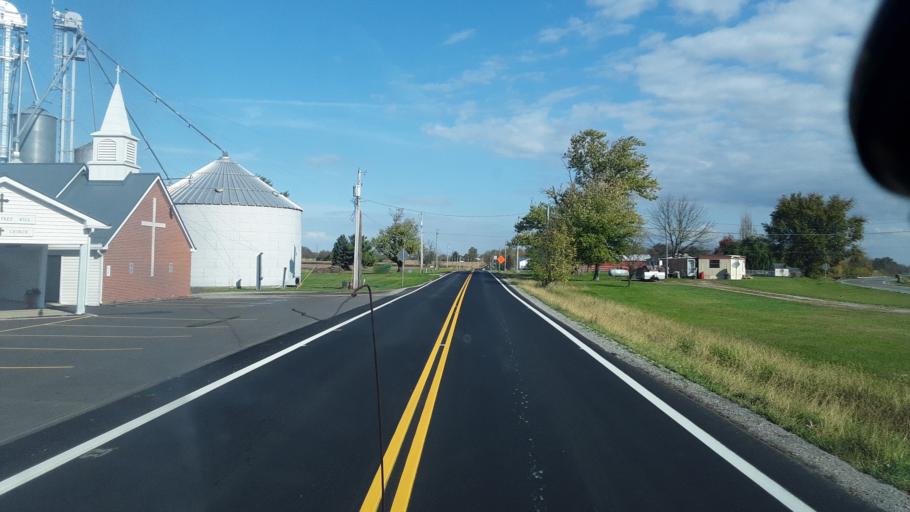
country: US
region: Ohio
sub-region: Highland County
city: Leesburg
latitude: 39.2909
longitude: -83.5910
